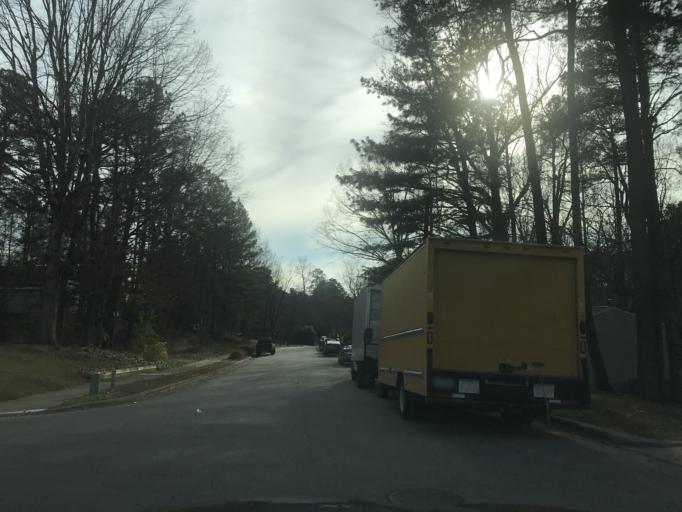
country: US
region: North Carolina
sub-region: Wake County
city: Raleigh
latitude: 35.8312
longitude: -78.5893
